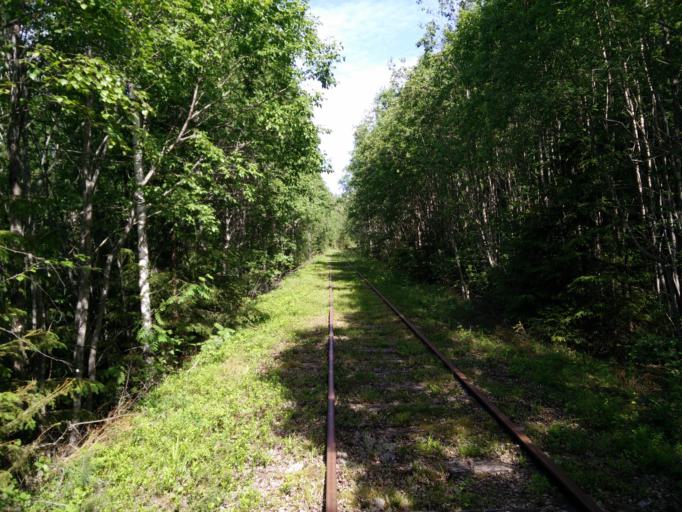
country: SE
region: Gaevleborg
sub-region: Hudiksvalls Kommun
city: Delsbo
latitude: 61.7973
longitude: 16.3749
